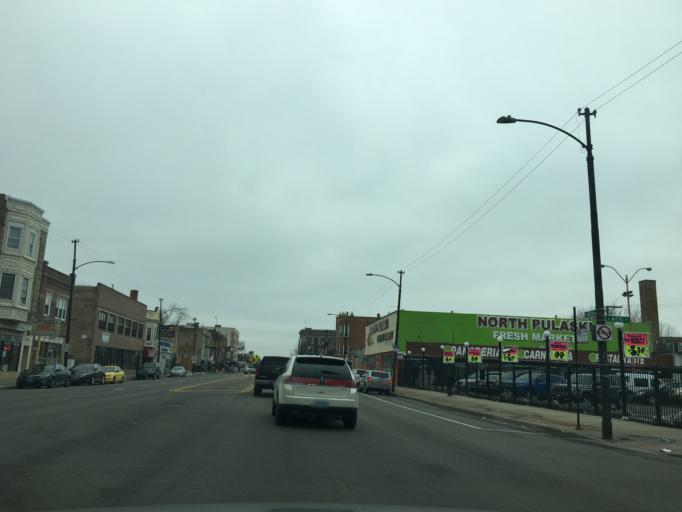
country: US
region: Illinois
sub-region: Cook County
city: Oak Park
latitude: 41.9100
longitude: -87.7226
